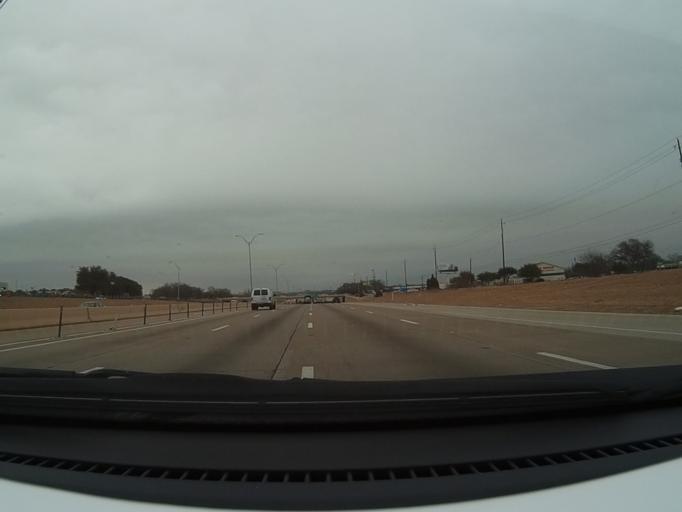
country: US
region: Texas
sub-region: Collin County
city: Plano
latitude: 33.0631
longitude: -96.6912
